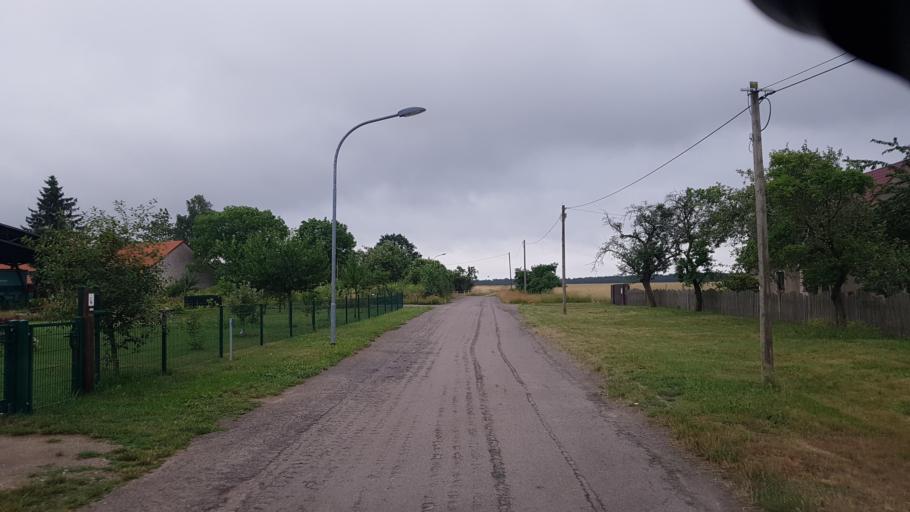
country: DE
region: Brandenburg
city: Juterbog
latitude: 51.9112
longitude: 13.1907
